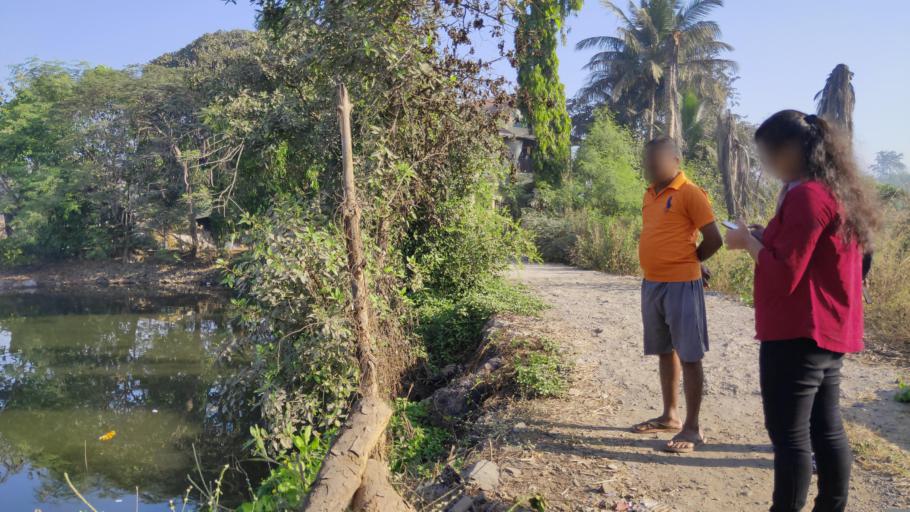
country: IN
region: Maharashtra
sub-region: Thane
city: Bhiwandi
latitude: 19.3225
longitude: 72.9628
